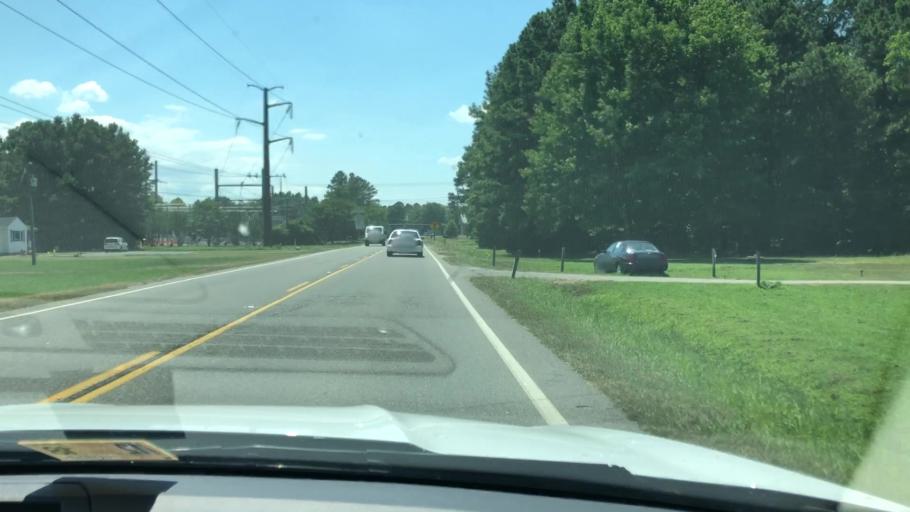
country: US
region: Virginia
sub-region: Middlesex County
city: Saluda
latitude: 37.5838
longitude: -76.4830
